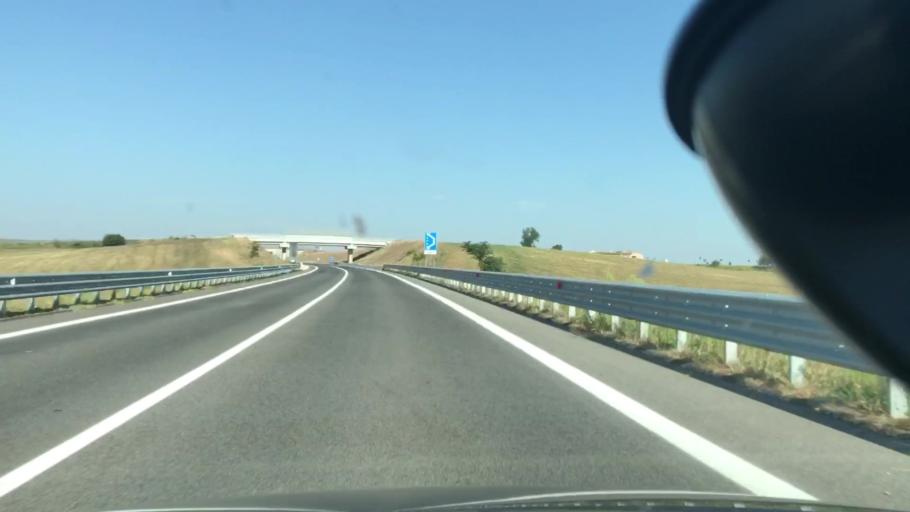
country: IT
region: Basilicate
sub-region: Provincia di Potenza
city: Palazzo San Gervasio
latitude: 40.9665
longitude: 16.0074
